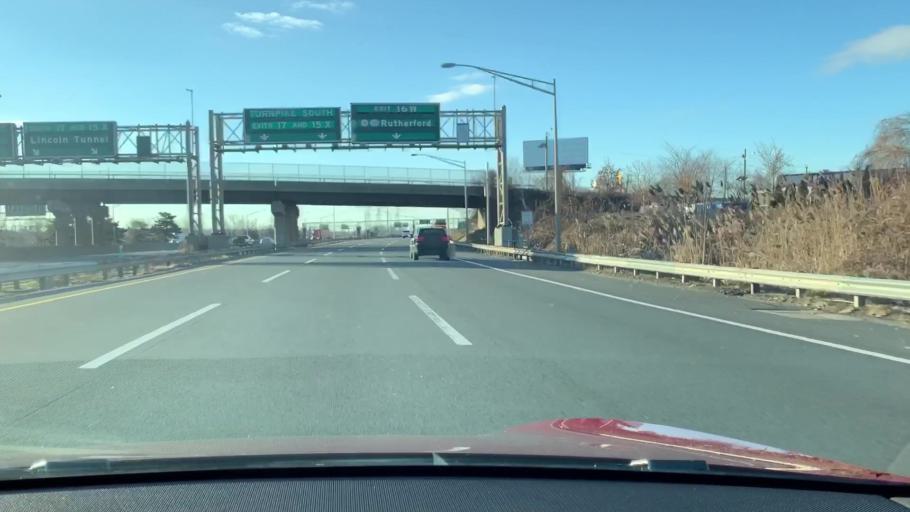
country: US
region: New Jersey
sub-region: Bergen County
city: Ridgefield
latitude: 40.8418
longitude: -74.0183
